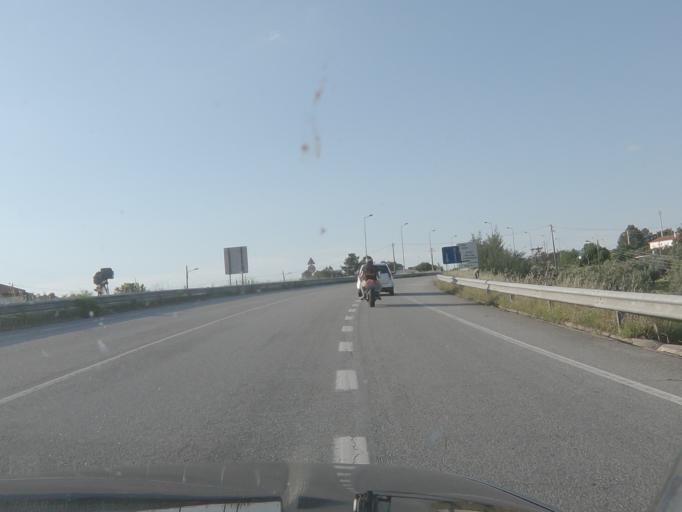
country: PT
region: Portalegre
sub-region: Portalegre
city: Portalegre
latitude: 39.3087
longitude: -7.4432
